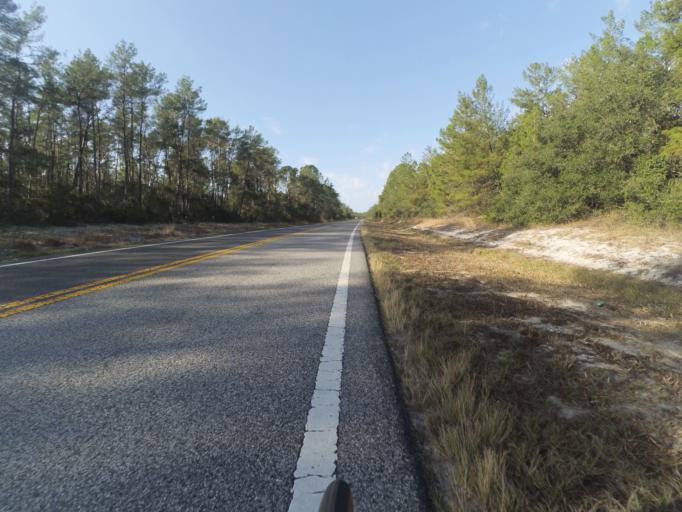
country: US
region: Florida
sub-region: Lake County
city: Astor
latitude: 29.1446
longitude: -81.5793
